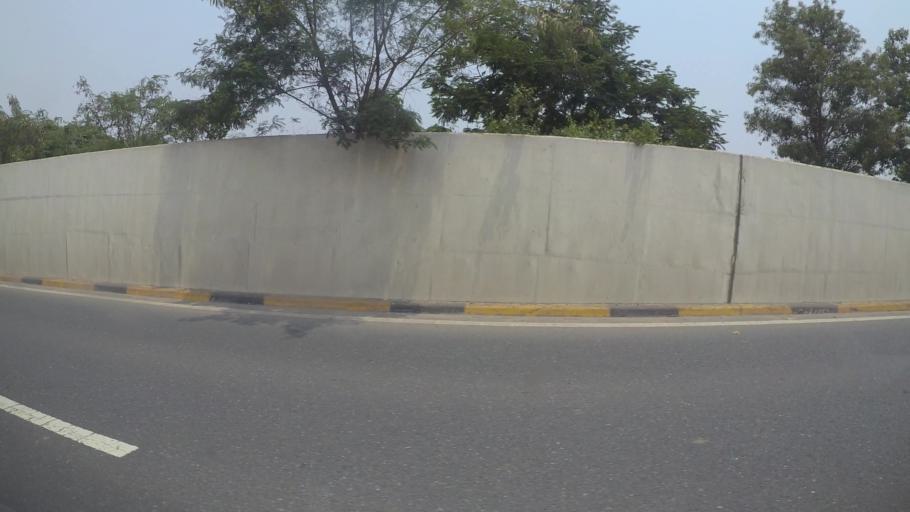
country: VN
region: Ha Noi
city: Cau Dien
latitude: 21.0096
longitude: 105.7429
